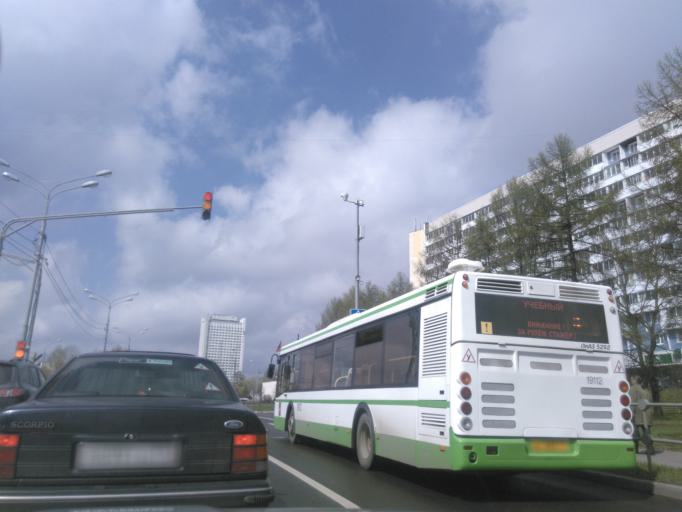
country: RU
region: Moskovskaya
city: Rzhavki
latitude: 55.9889
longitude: 37.2270
